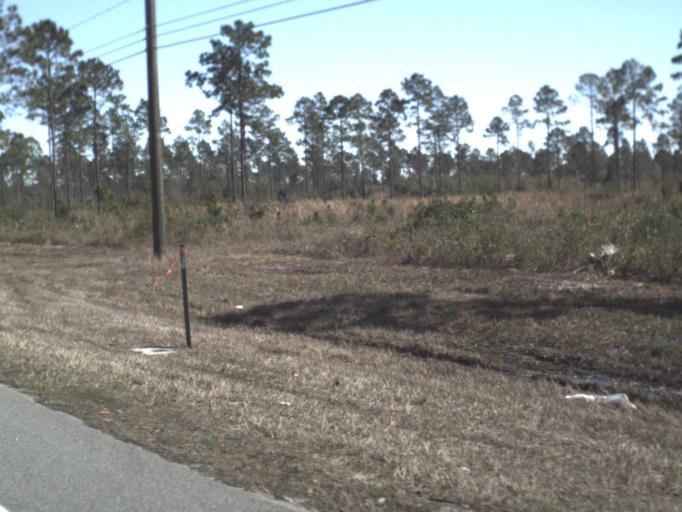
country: US
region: Florida
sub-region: Bay County
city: Panama City Beach
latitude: 30.3211
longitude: -85.8004
